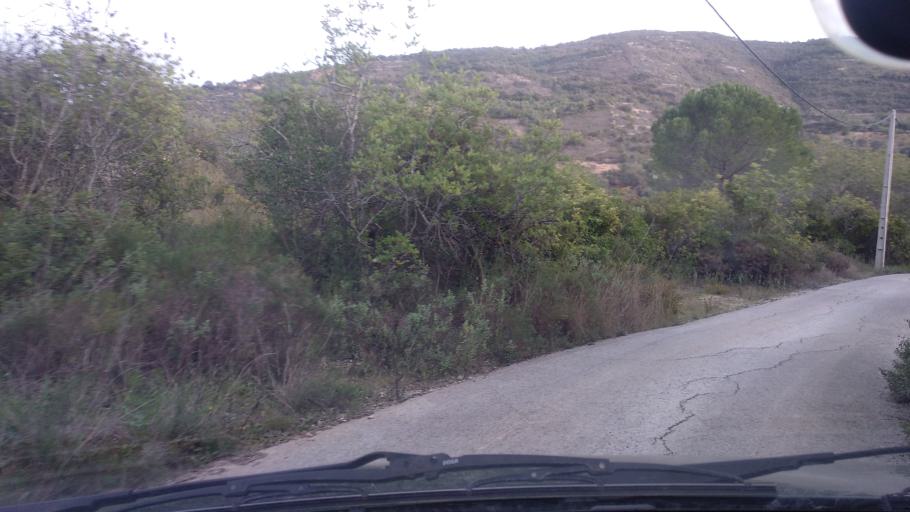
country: PT
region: Faro
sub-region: Sao Bras de Alportel
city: Sao Bras de Alportel
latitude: 37.1228
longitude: -7.9043
